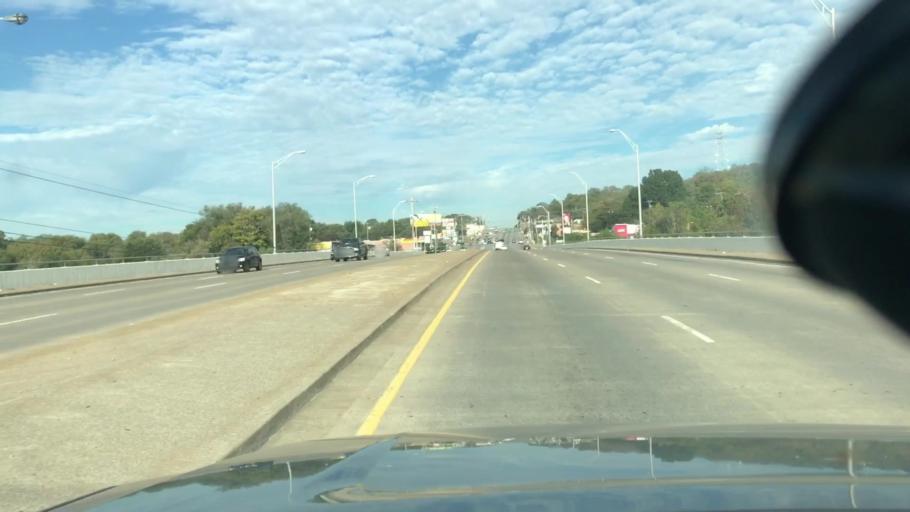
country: US
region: Tennessee
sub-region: Davidson County
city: Nashville
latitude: 36.1909
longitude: -86.8264
